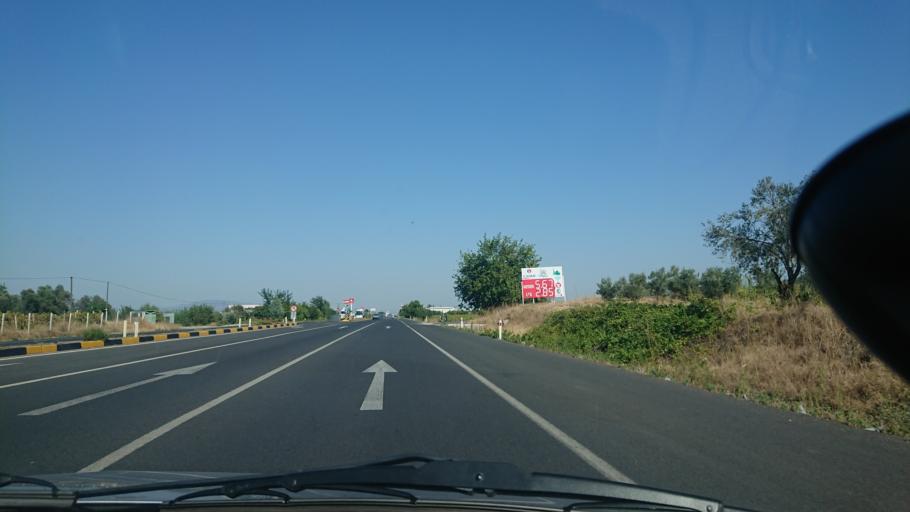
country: TR
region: Manisa
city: Ahmetli
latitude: 38.5072
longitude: 27.8930
